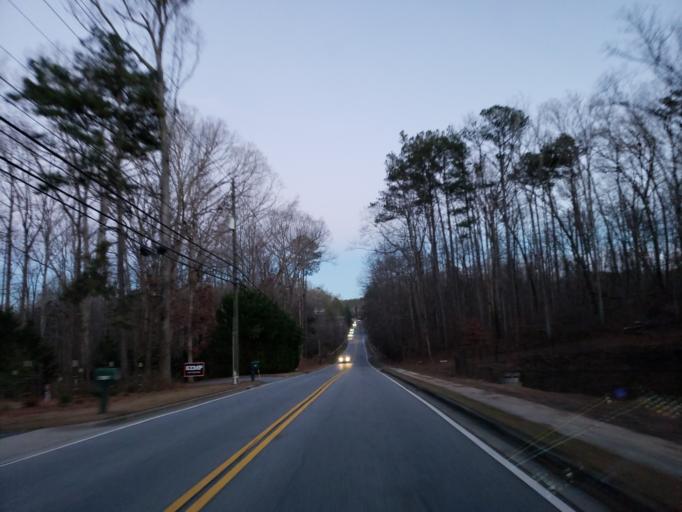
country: US
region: Georgia
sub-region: Cobb County
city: Kennesaw
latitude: 33.9658
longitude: -84.6951
